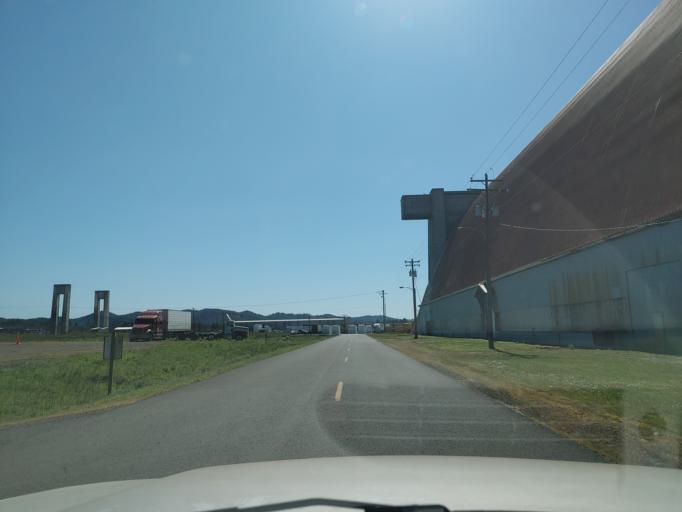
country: US
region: Oregon
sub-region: Tillamook County
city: Tillamook
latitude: 45.4200
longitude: -123.8042
